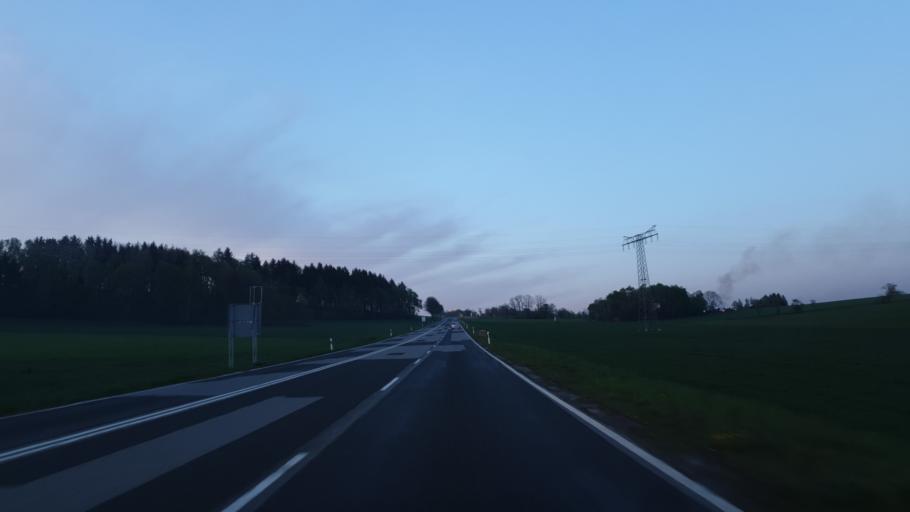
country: DE
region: Saxony
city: Lossnitz
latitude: 50.6421
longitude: 12.7384
